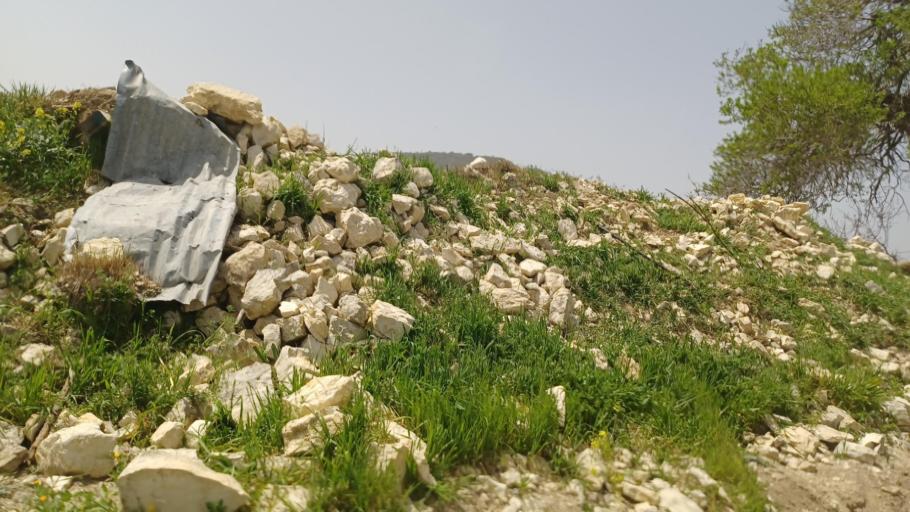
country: CY
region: Limassol
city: Pachna
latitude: 34.7826
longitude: 32.7511
